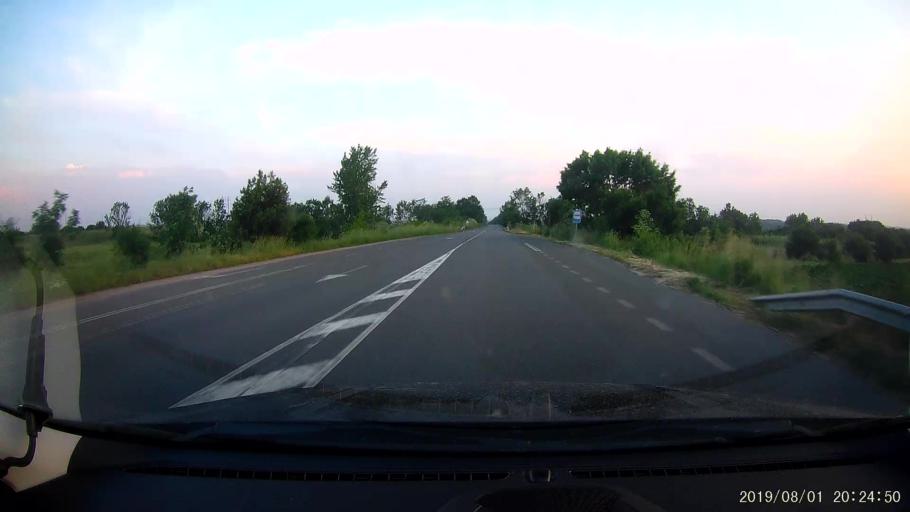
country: BG
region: Yambol
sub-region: Obshtina Elkhovo
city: Elkhovo
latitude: 42.2254
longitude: 26.5911
